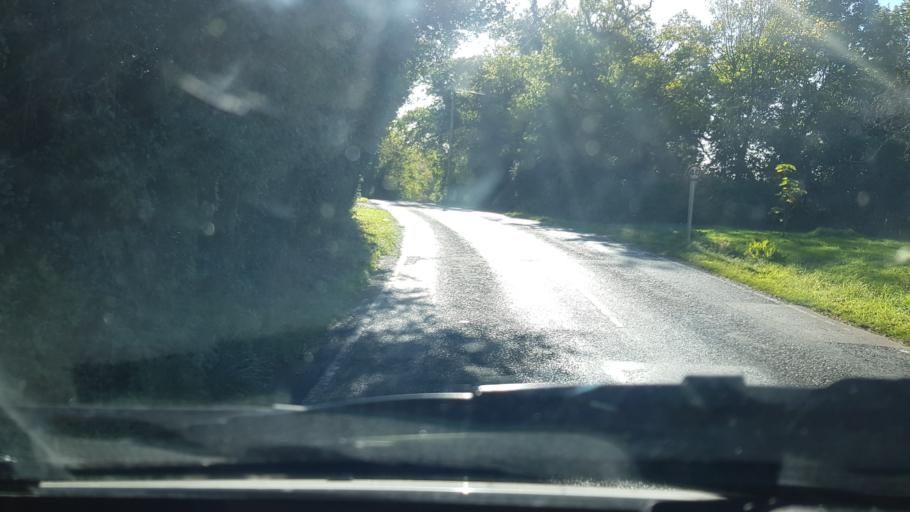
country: GB
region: England
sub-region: Surrey
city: Cranleigh
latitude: 51.1539
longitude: -0.4902
